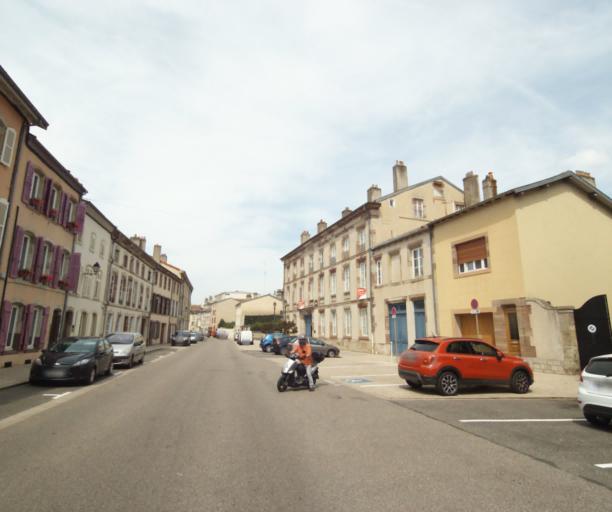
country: FR
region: Lorraine
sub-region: Departement de Meurthe-et-Moselle
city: Luneville
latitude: 48.5936
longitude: 6.4963
